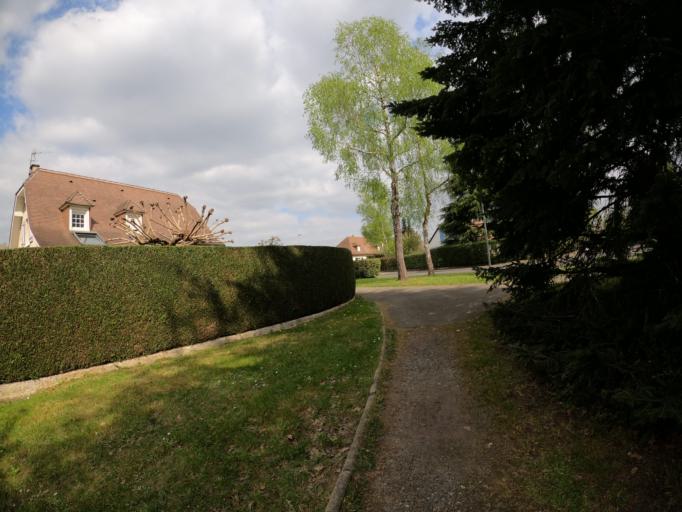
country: FR
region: Aquitaine
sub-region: Departement des Pyrenees-Atlantiques
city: Lons
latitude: 43.3251
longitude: -0.3900
